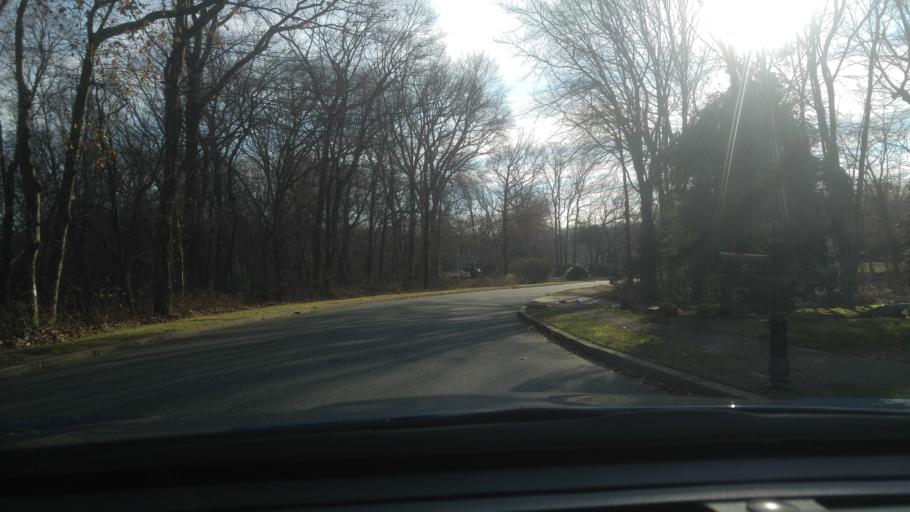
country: US
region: Rhode Island
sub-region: Kent County
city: East Greenwich
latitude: 41.6836
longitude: -71.4717
